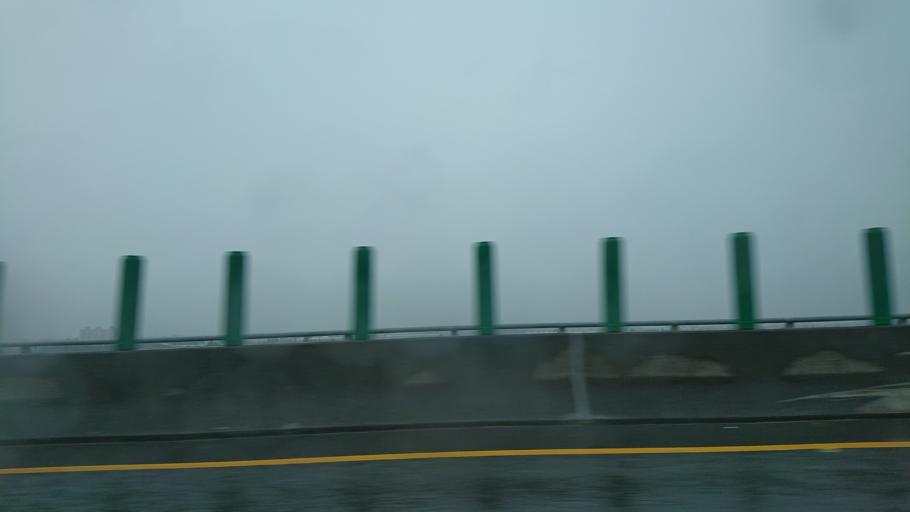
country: TW
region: Taiwan
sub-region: Yunlin
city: Douliu
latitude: 23.7859
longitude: 120.2752
